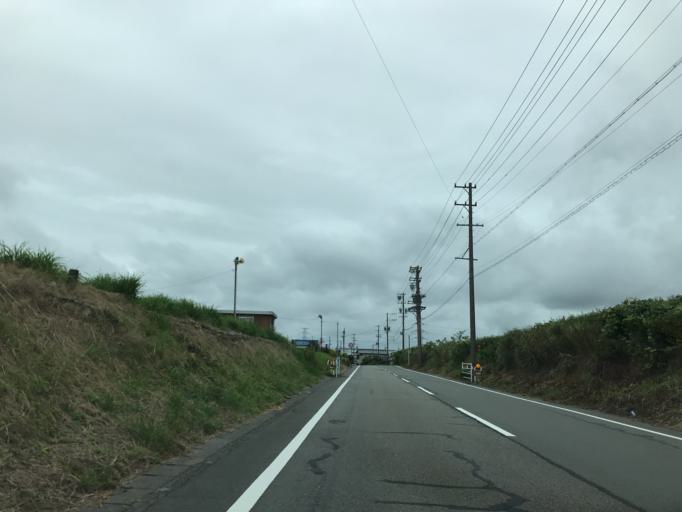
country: JP
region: Shizuoka
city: Kanaya
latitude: 34.7652
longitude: 138.1367
